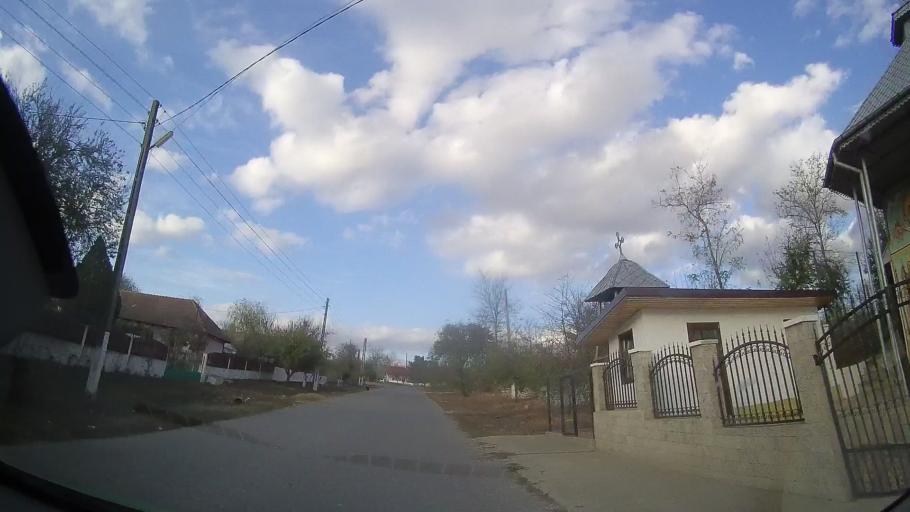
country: RO
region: Constanta
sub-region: Comuna Cerchezu
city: Cerchezu
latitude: 43.8597
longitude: 28.1014
